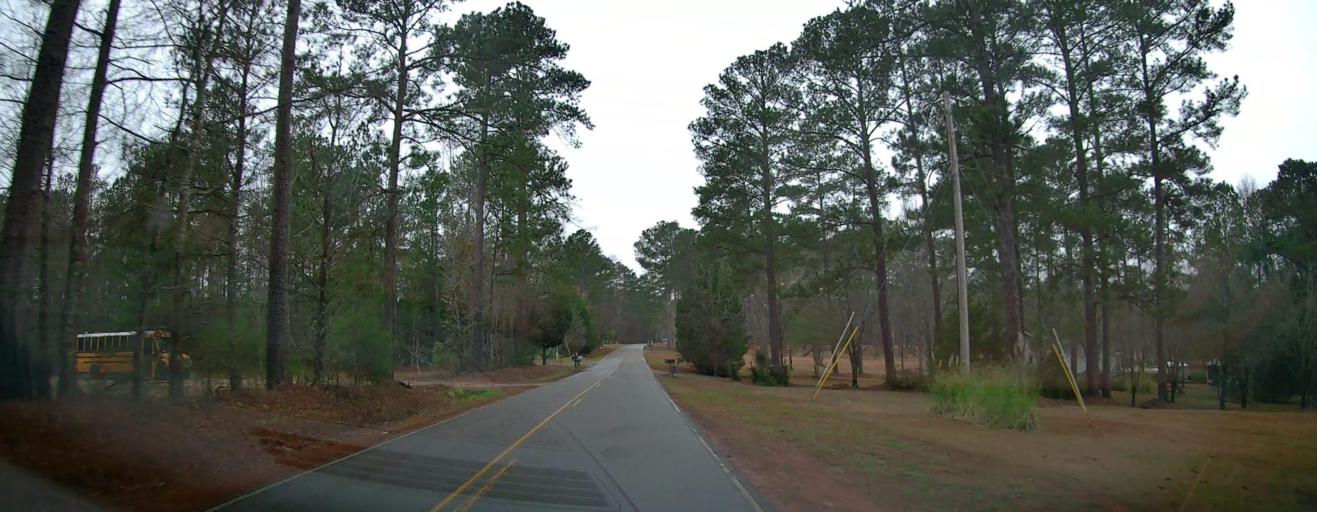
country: US
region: Georgia
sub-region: Monroe County
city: Forsyth
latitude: 33.0186
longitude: -83.8502
